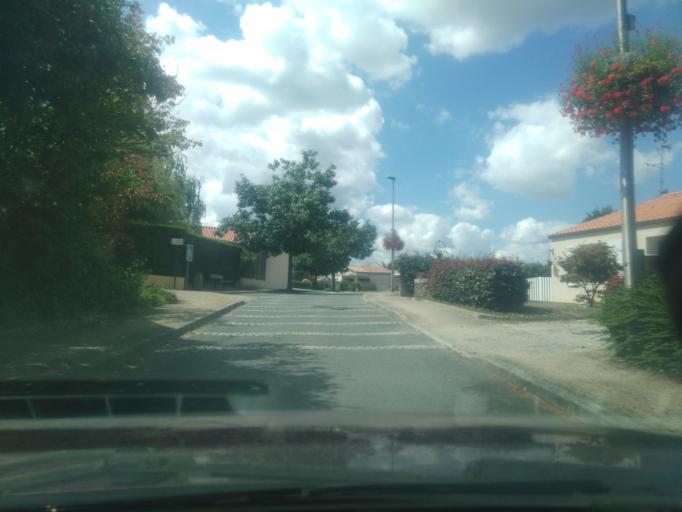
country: FR
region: Pays de la Loire
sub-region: Departement de la Vendee
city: Chauche
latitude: 46.8292
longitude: -1.2708
